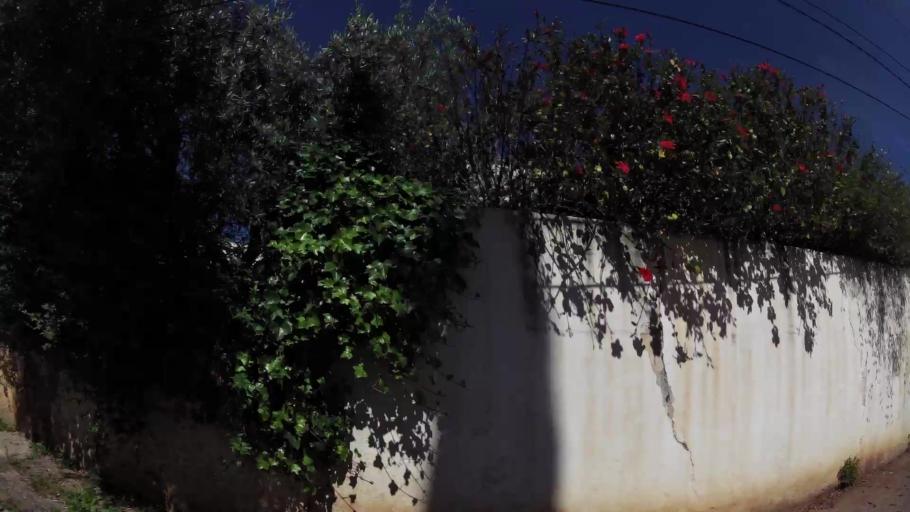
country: MA
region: Fes-Boulemane
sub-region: Fes
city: Fes
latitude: 34.0188
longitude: -4.9901
